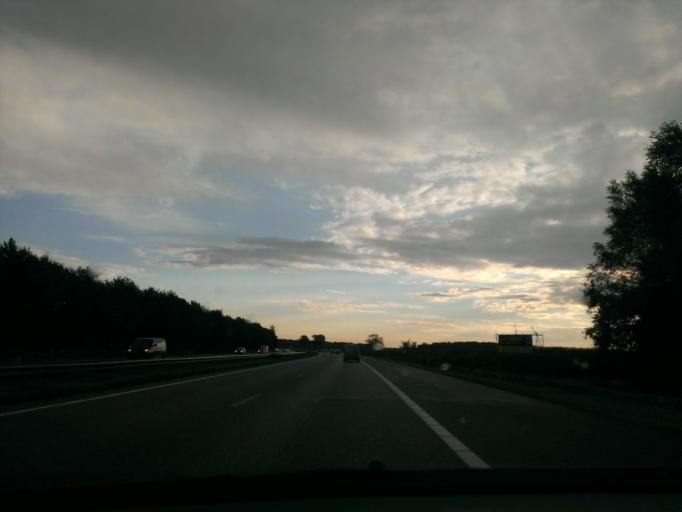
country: NL
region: Drenthe
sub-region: Gemeente De Wolden
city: Ruinen
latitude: 52.6888
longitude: 6.3973
